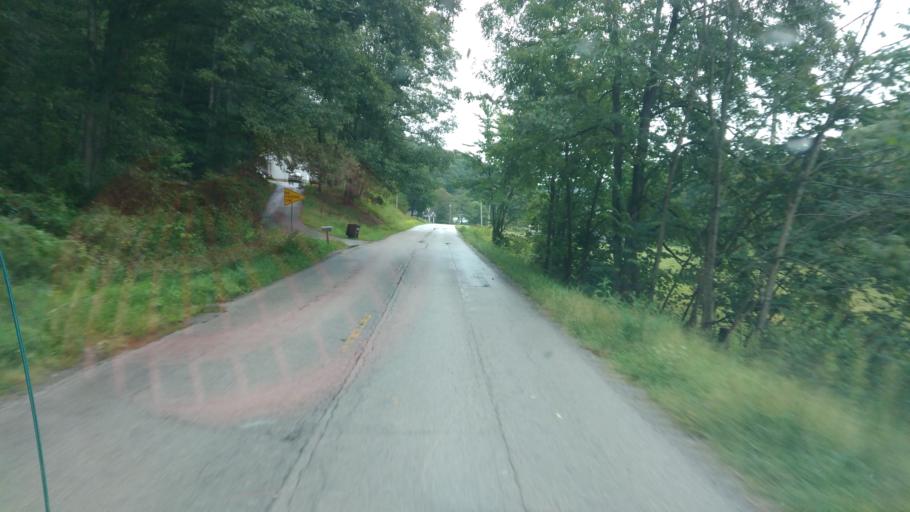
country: US
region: Kentucky
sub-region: Fleming County
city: Flemingsburg
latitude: 38.4482
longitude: -83.5071
